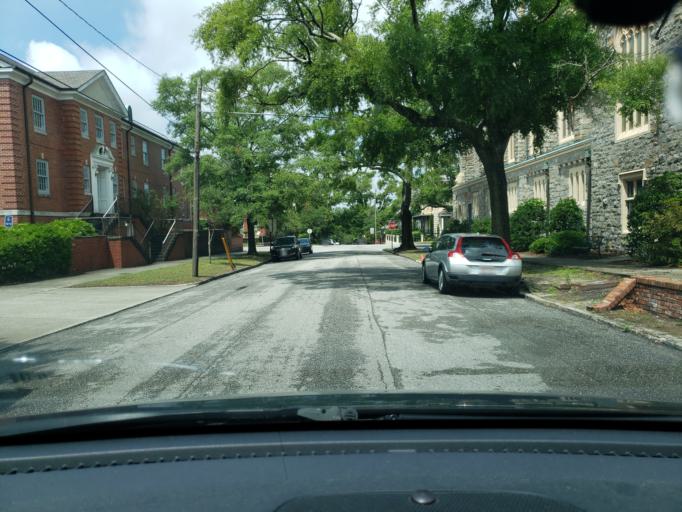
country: US
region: North Carolina
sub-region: New Hanover County
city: Wilmington
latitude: 34.2331
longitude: -77.9450
